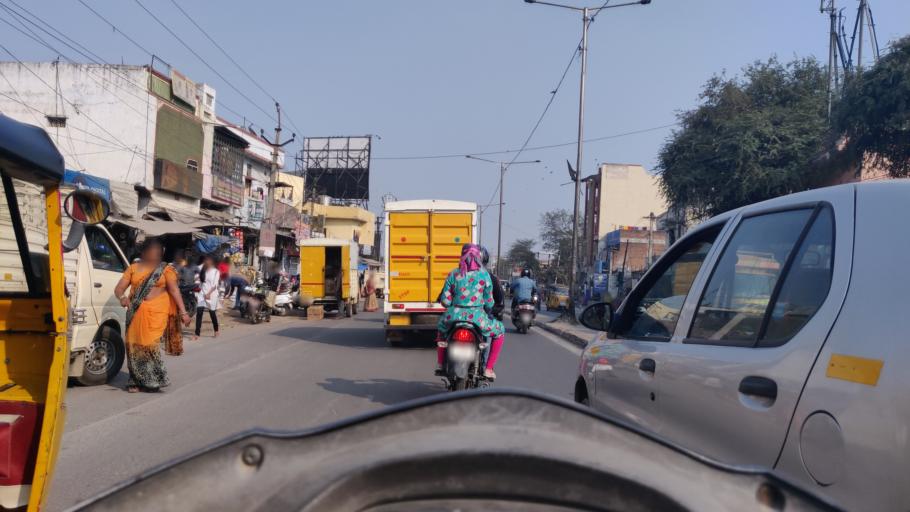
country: IN
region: Telangana
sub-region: Rangareddi
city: Uppal Kalan
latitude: 17.4015
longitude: 78.5700
